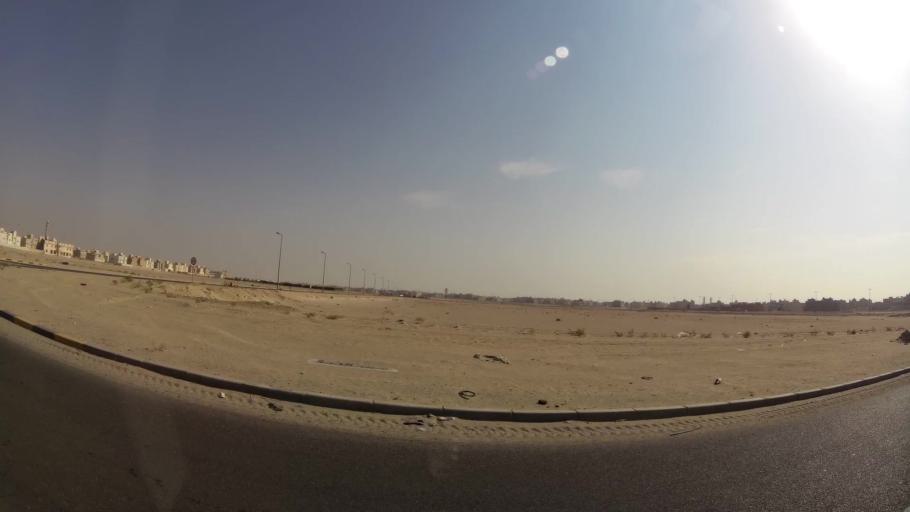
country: KW
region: Al Ahmadi
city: Al Wafrah
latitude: 28.7850
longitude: 48.0692
